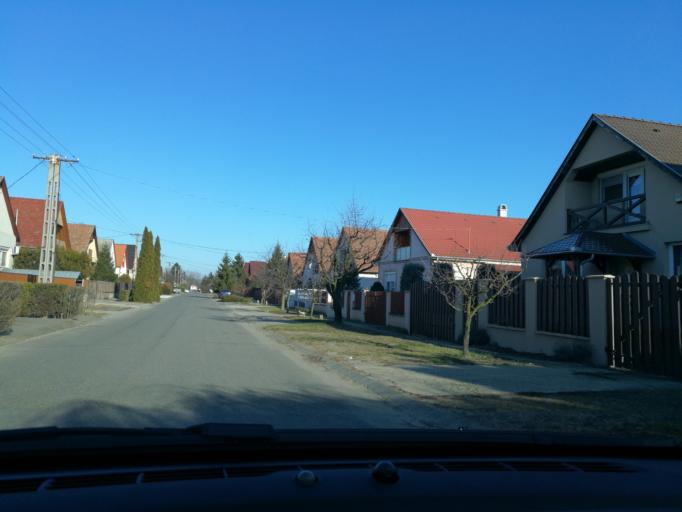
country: HU
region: Szabolcs-Szatmar-Bereg
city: Nyiregyhaza
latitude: 47.9259
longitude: 21.7567
